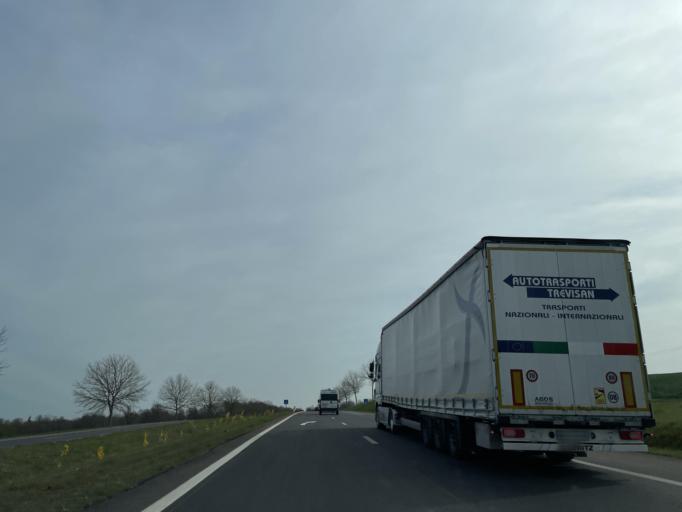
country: FR
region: Champagne-Ardenne
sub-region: Departement de l'Aube
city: Villenauxe-la-Grande
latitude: 48.5082
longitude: 3.5835
